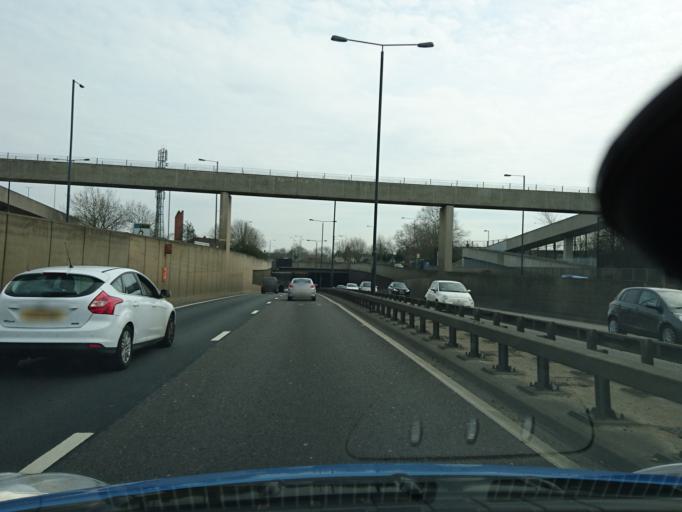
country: GB
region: England
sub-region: Greater London
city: Walthamstow
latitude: 51.6027
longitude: -0.0200
